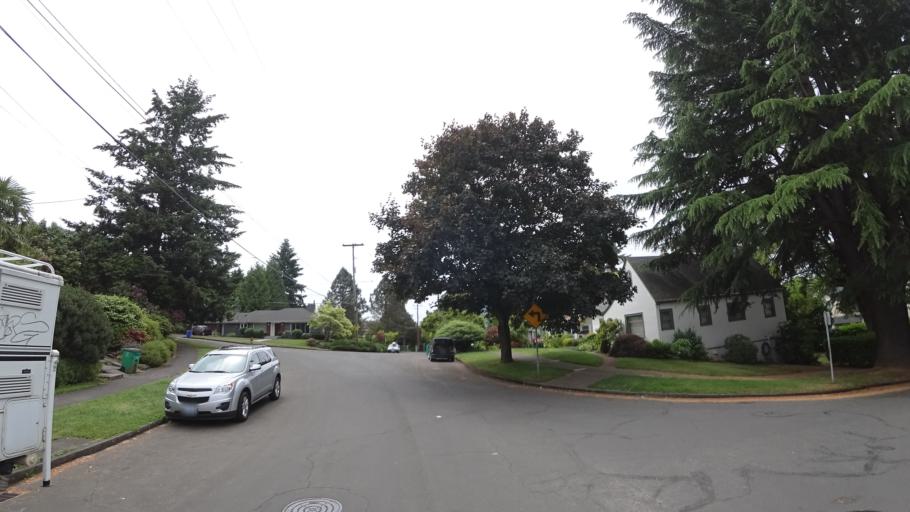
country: US
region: Oregon
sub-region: Multnomah County
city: Portland
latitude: 45.5316
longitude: -122.6127
